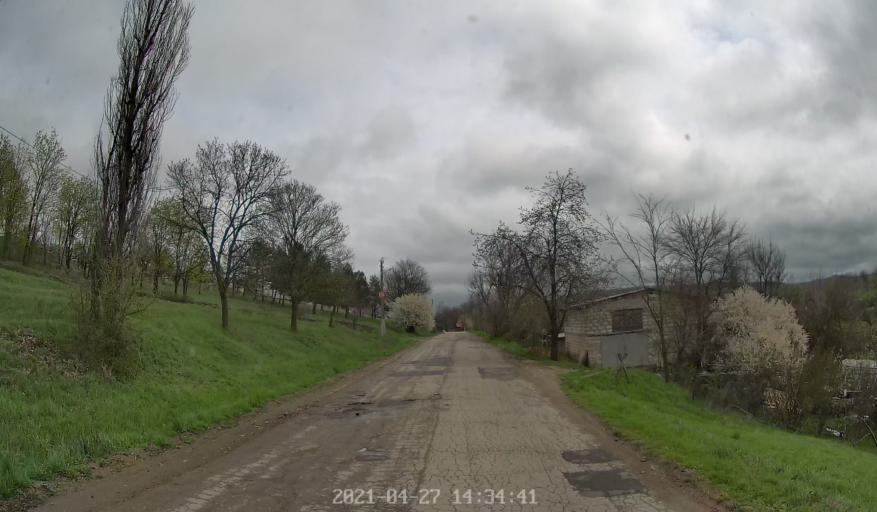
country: MD
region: Chisinau
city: Vadul lui Voda
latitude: 47.0557
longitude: 29.0324
